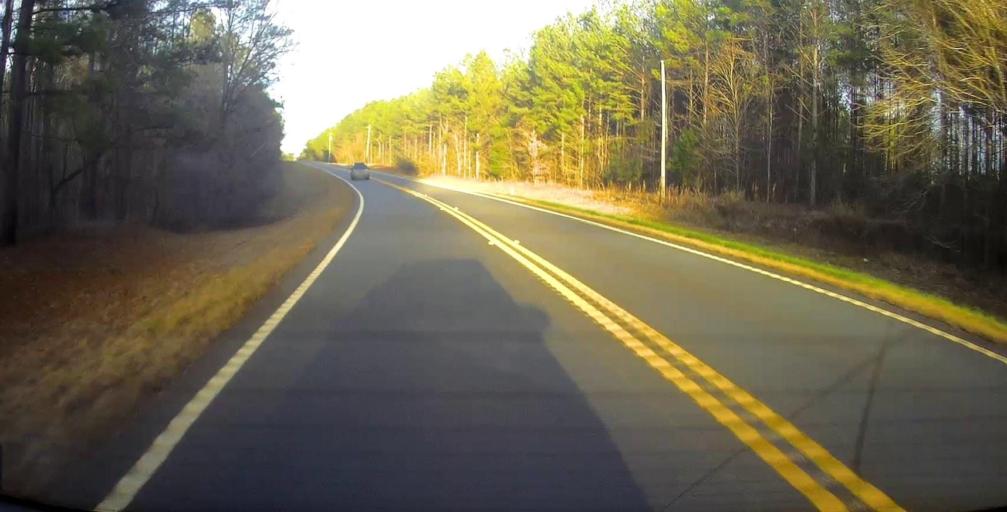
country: US
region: Georgia
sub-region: Talbot County
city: Sardis
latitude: 32.7255
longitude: -84.6288
